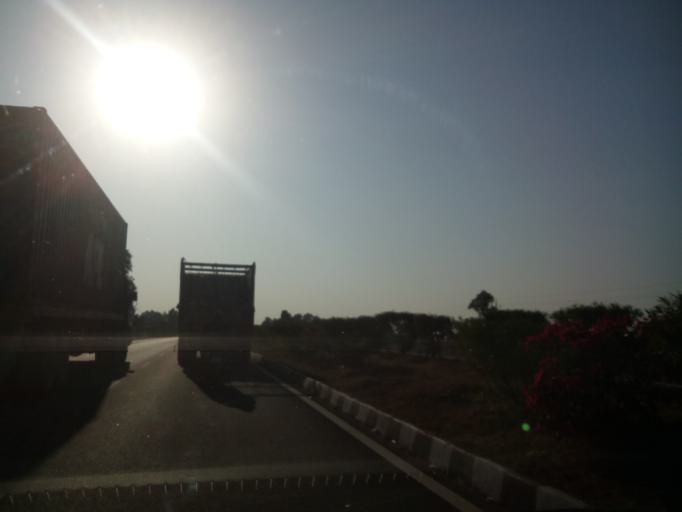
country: IN
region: Rajasthan
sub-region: Sirohi
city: Abu Road
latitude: 24.3739
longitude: 72.5896
